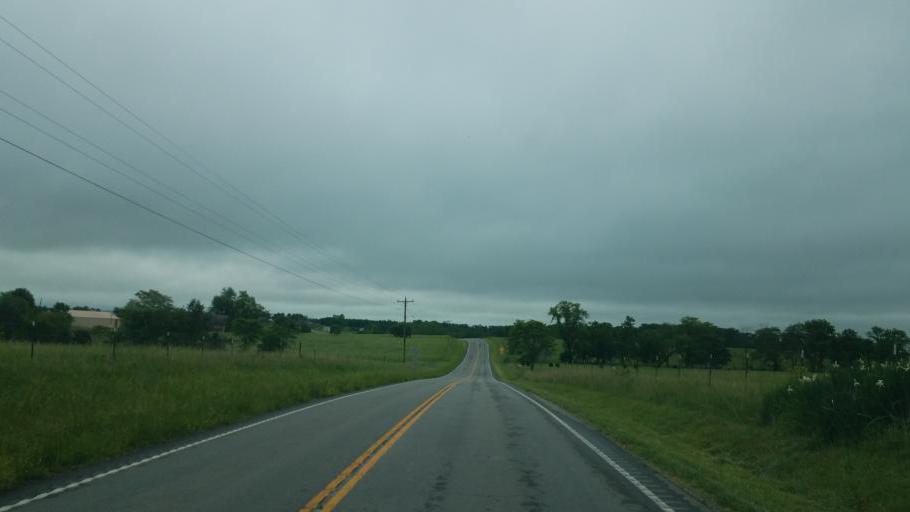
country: US
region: Missouri
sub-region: Moniteau County
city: California
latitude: 38.5305
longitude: -92.5760
